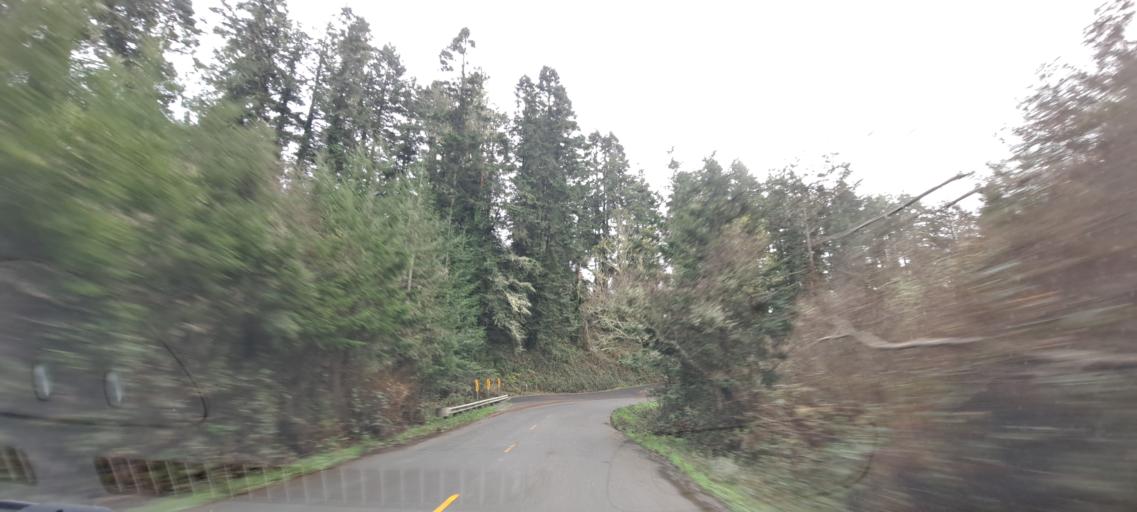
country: US
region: California
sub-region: Humboldt County
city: Fortuna
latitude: 40.5982
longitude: -124.1402
